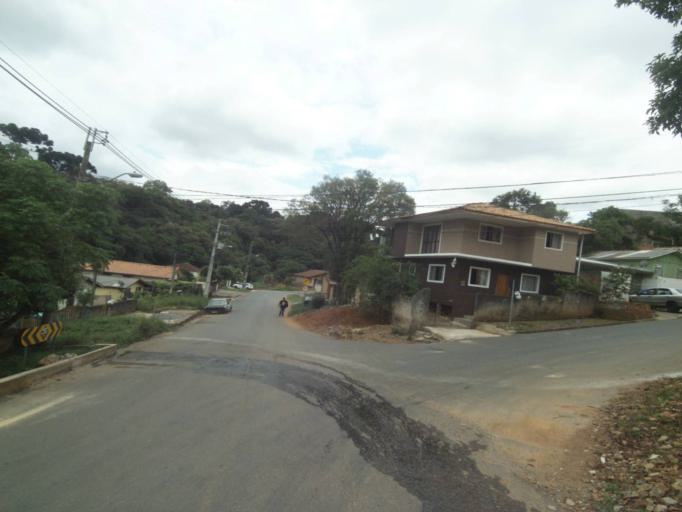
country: BR
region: Parana
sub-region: Curitiba
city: Curitiba
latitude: -25.3879
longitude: -49.2949
